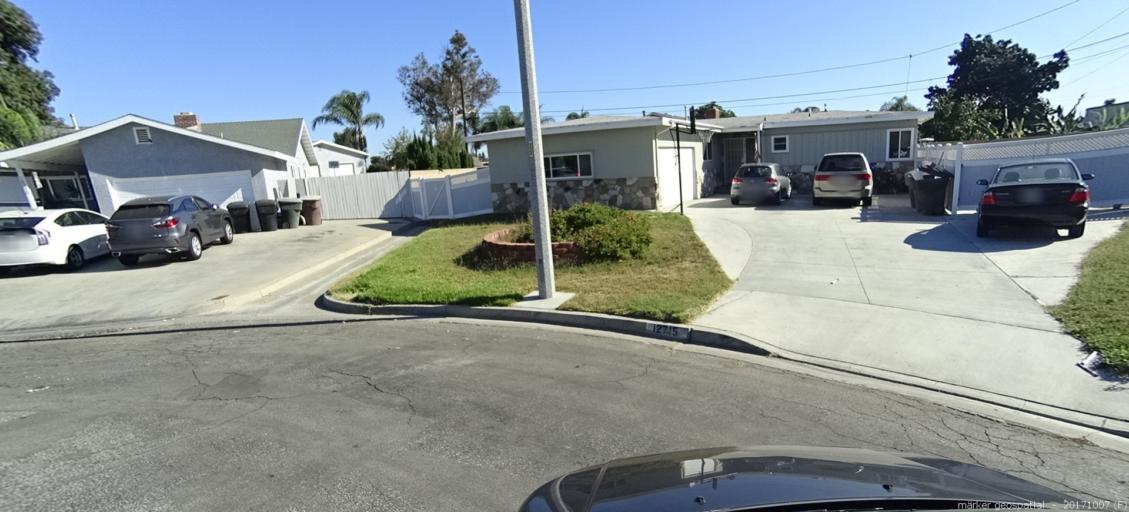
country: US
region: California
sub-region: Orange County
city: Stanton
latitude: 33.7778
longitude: -117.9780
